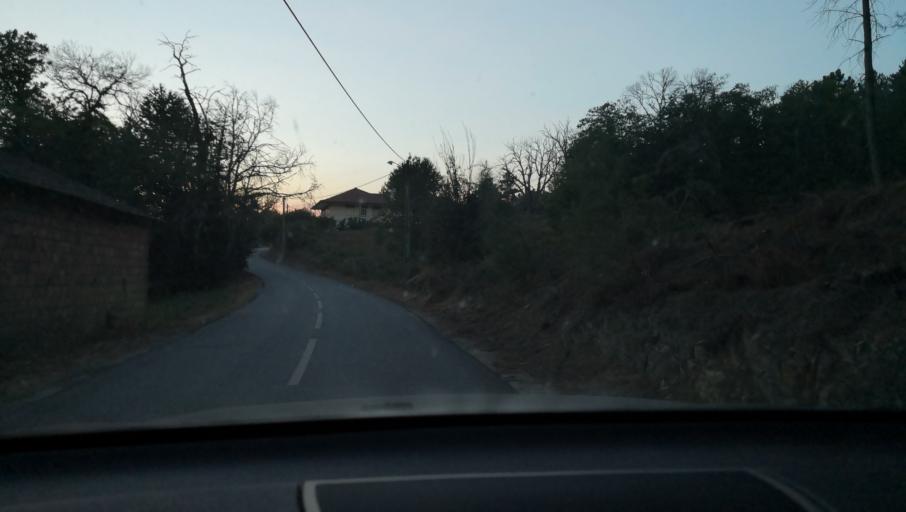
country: PT
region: Vila Real
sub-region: Sabrosa
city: Vilela
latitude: 41.2407
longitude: -7.6145
